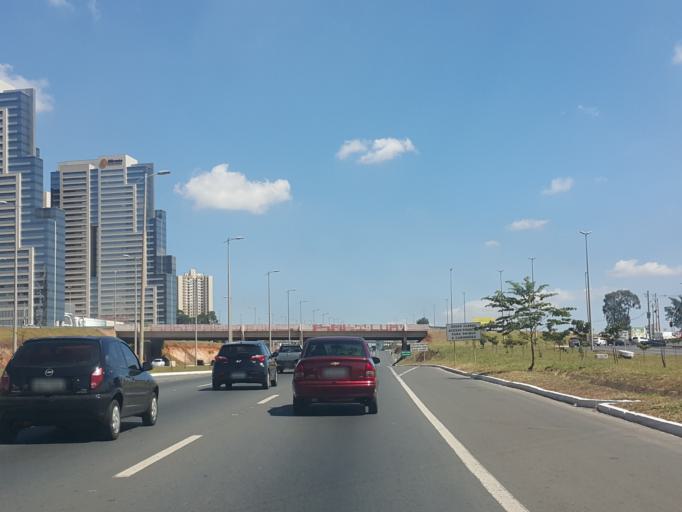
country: BR
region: Federal District
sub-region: Brasilia
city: Brasilia
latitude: -15.8299
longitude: -48.0371
